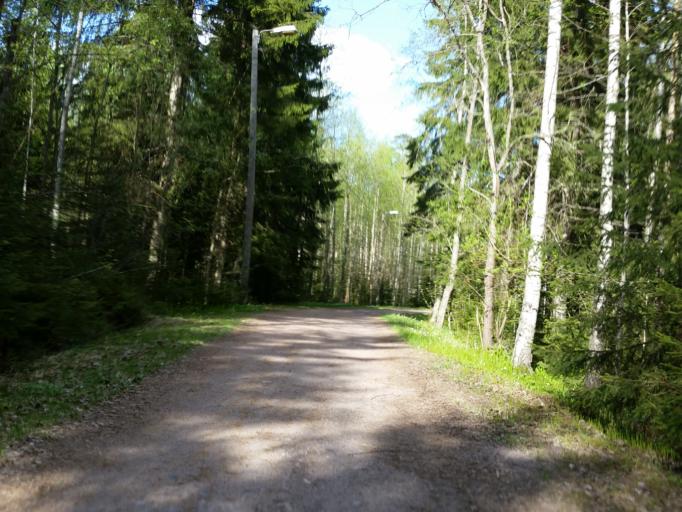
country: FI
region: Uusimaa
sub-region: Helsinki
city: Kauniainen
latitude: 60.1838
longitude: 24.7094
